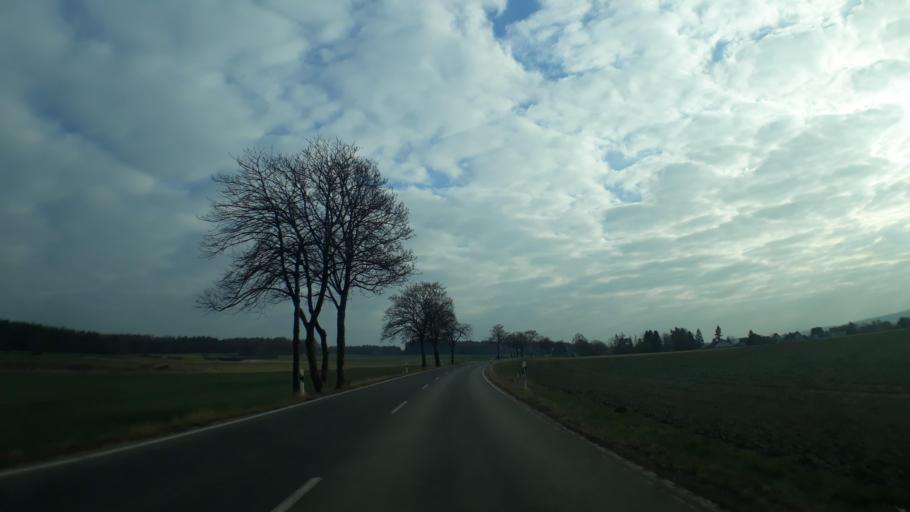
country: DE
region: North Rhine-Westphalia
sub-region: Regierungsbezirk Koln
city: Bad Munstereifel
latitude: 50.6106
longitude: 6.7385
